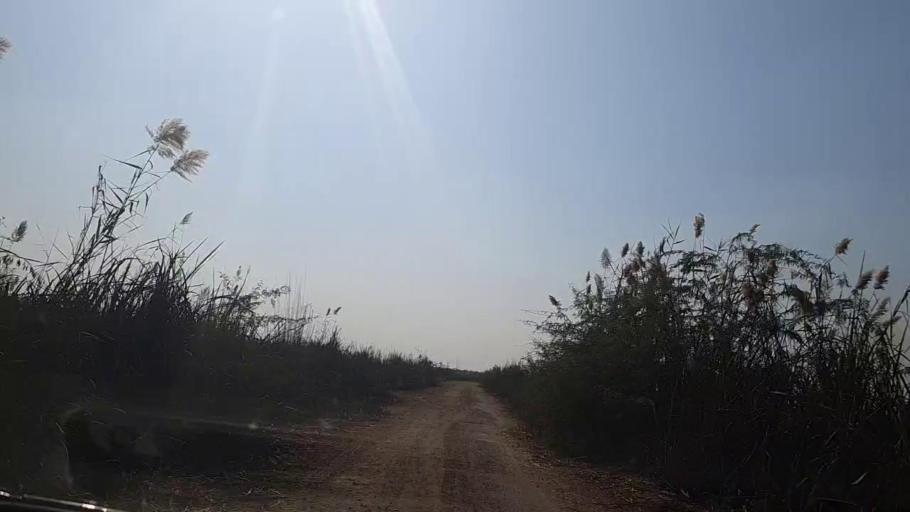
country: PK
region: Sindh
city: Sakrand
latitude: 26.0725
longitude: 68.3686
